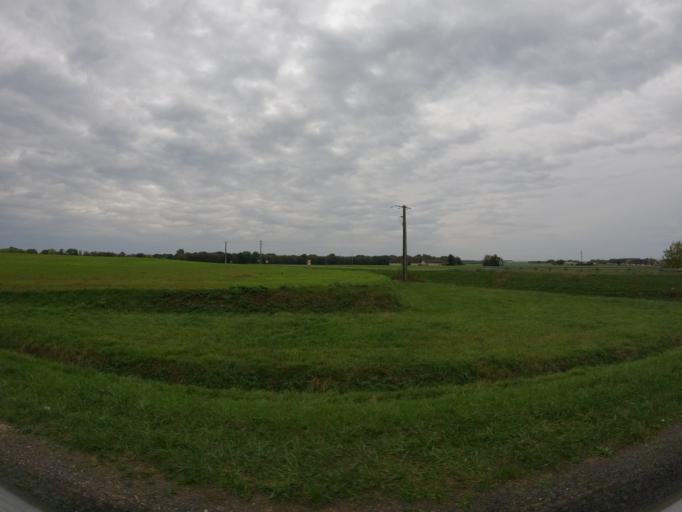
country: FR
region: Ile-de-France
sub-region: Departement de Seine-et-Marne
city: Chanteloup-en-Brie
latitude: 48.8289
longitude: 2.7564
